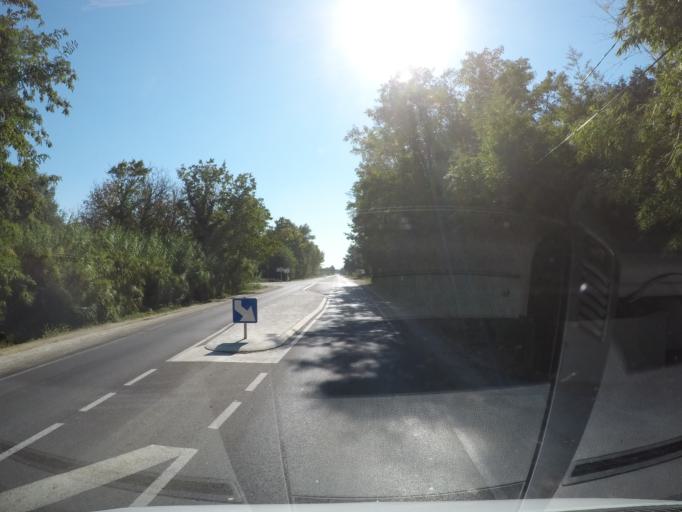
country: FR
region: Languedoc-Roussillon
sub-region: Departement du Gard
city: Moussac
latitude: 43.9706
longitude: 4.2210
